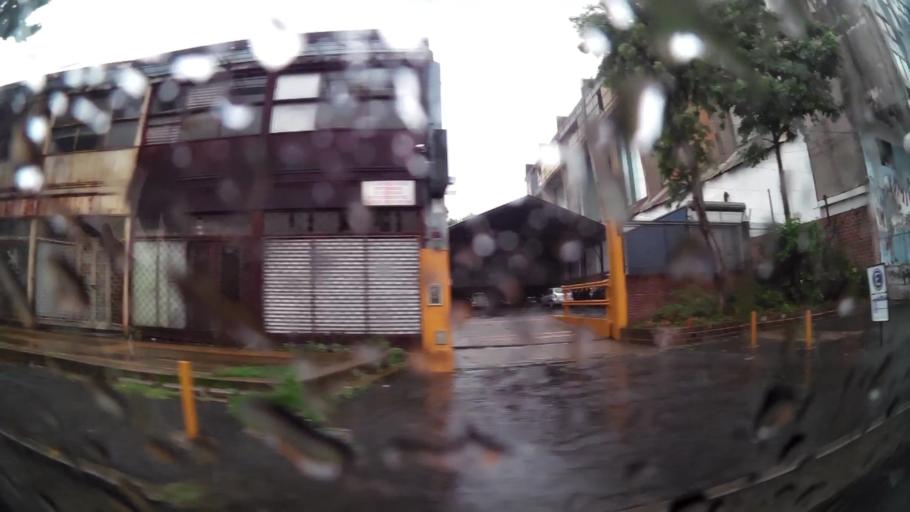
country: AR
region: Buenos Aires
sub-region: Partido de Avellaneda
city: Avellaneda
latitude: -34.6406
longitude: -58.3615
